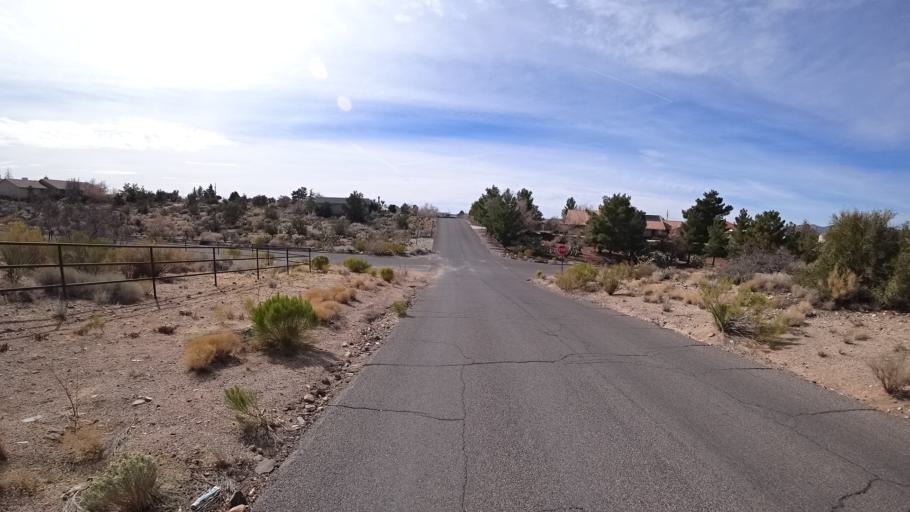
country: US
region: Arizona
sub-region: Mohave County
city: Kingman
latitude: 35.1873
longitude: -113.9879
